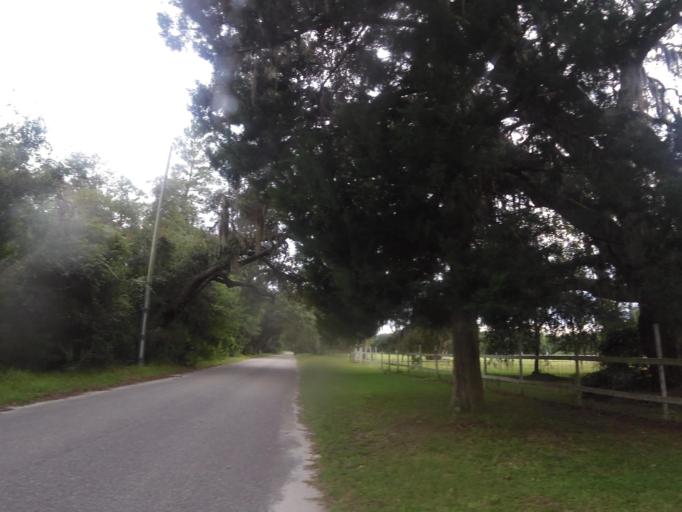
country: US
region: Florida
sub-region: Flagler County
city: Bunnell
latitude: 29.5168
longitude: -81.3122
